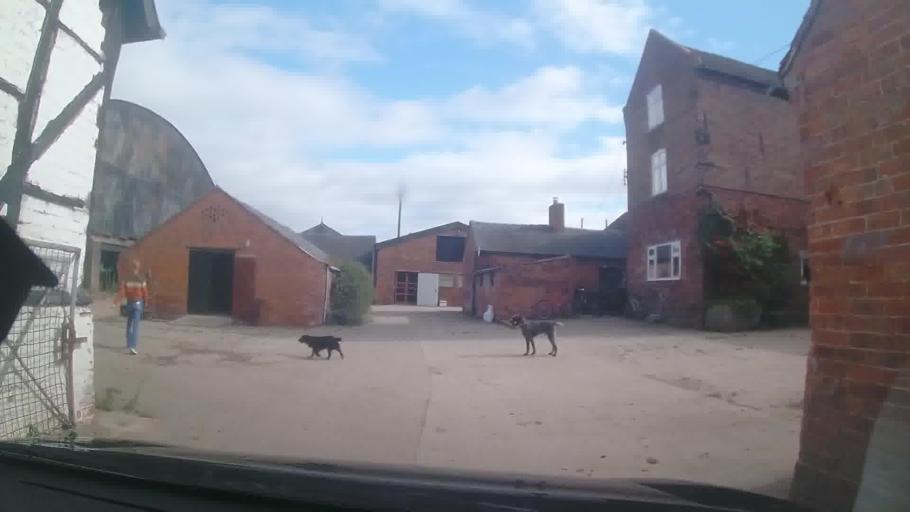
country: GB
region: England
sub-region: Shropshire
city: Prees
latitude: 52.8736
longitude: -2.6318
